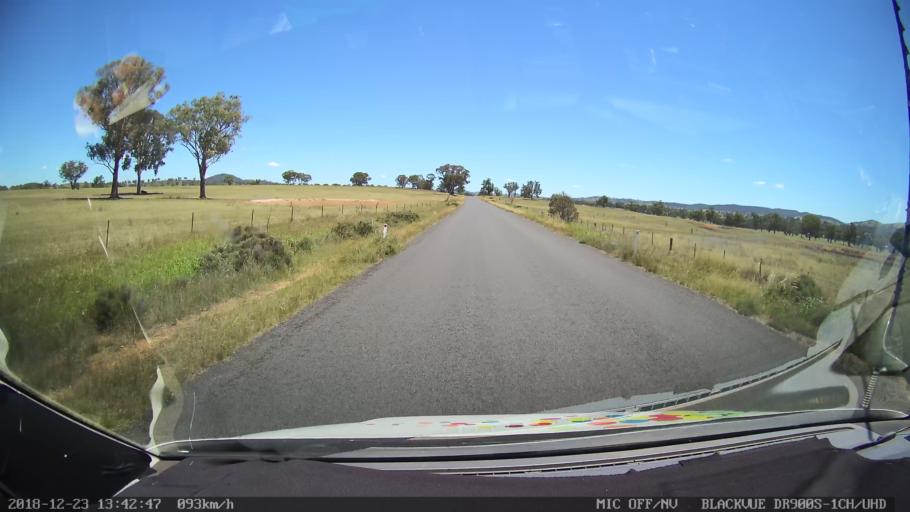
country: AU
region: New South Wales
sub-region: Armidale Dumaresq
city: Armidale
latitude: -30.4806
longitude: 151.1587
